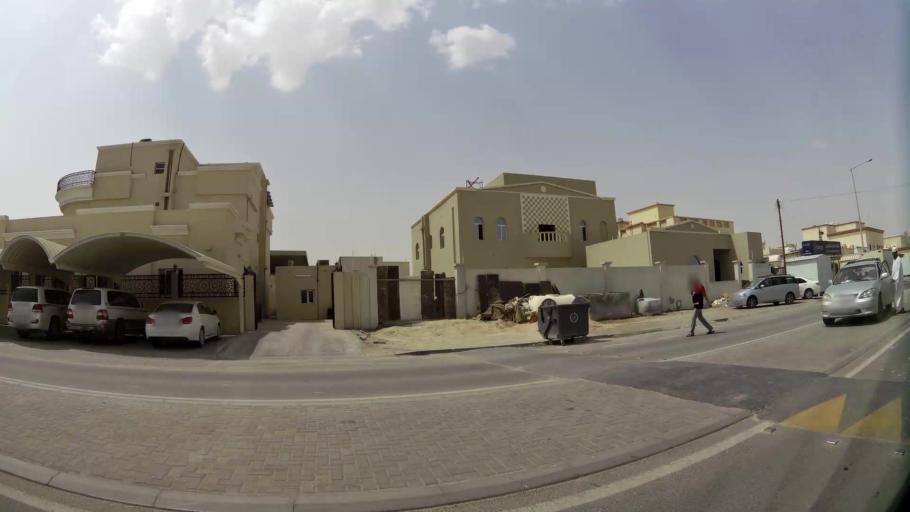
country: QA
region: Baladiyat ar Rayyan
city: Ar Rayyan
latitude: 25.2315
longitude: 51.4274
